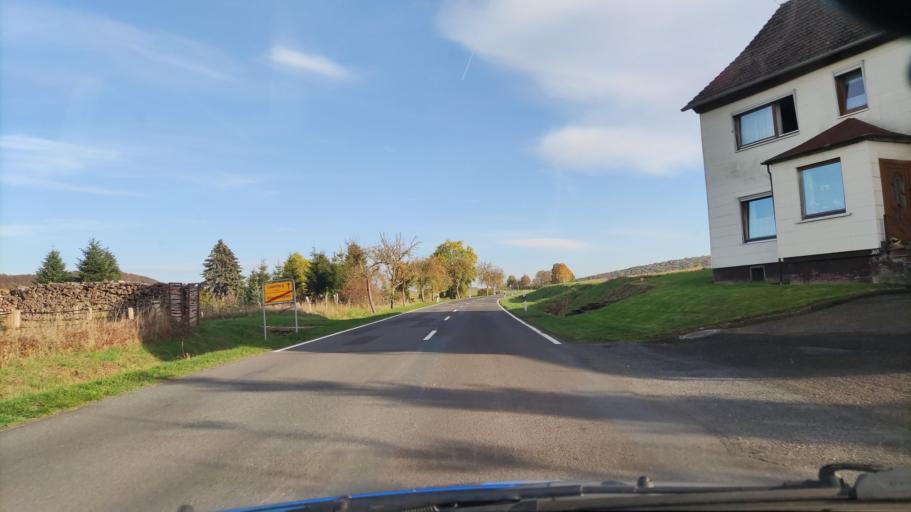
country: DE
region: Lower Saxony
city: Dassel
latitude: 51.7721
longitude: 9.7248
